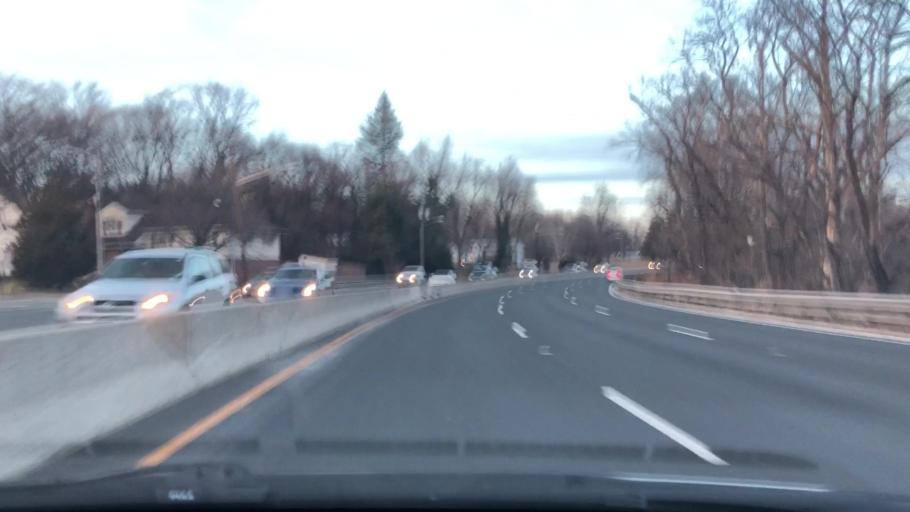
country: US
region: New Jersey
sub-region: Bergen County
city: Elmwood Park
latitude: 40.9122
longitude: -74.1344
